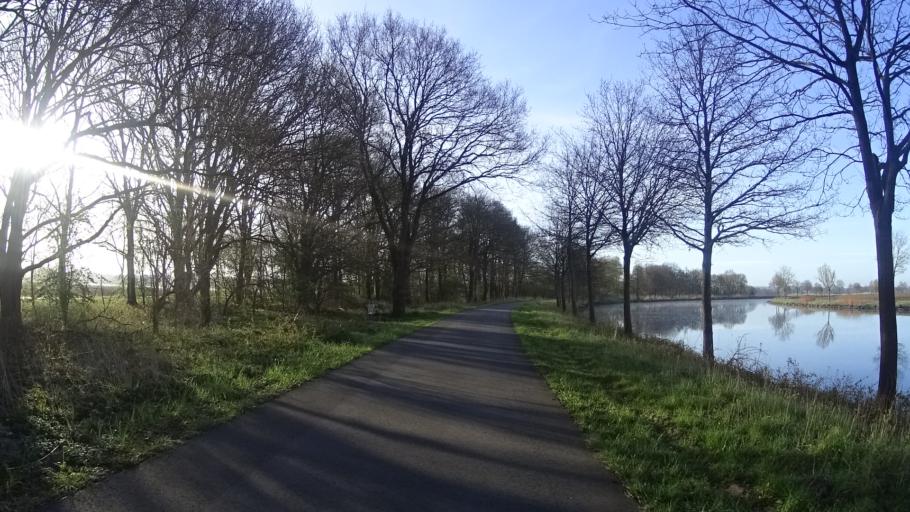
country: DE
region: Lower Saxony
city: Lathen
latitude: 52.8543
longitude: 7.3054
